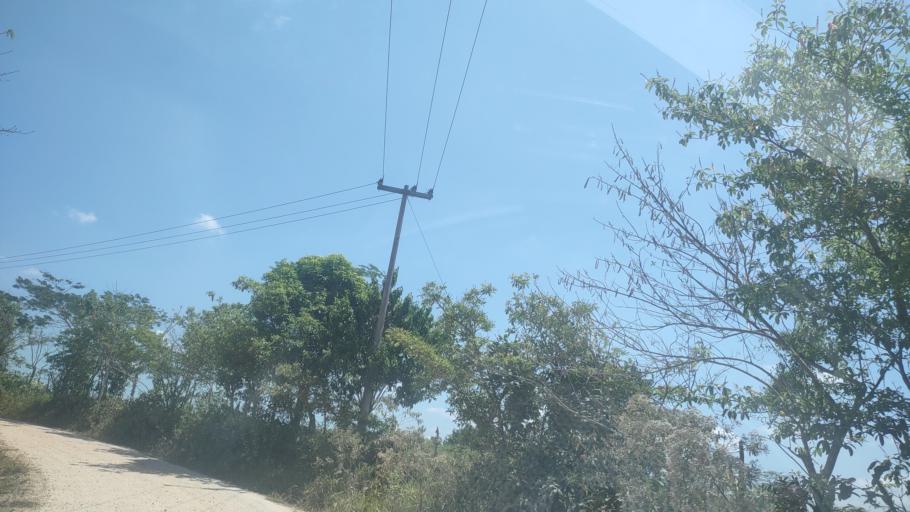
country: MX
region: Veracruz
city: Las Choapas
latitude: 17.7846
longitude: -94.1378
